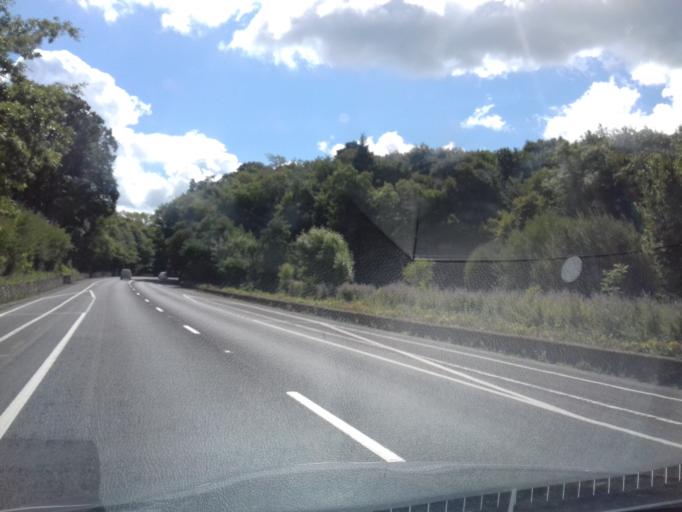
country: IE
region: Munster
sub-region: Waterford
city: Waterford
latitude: 52.2135
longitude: -7.1212
